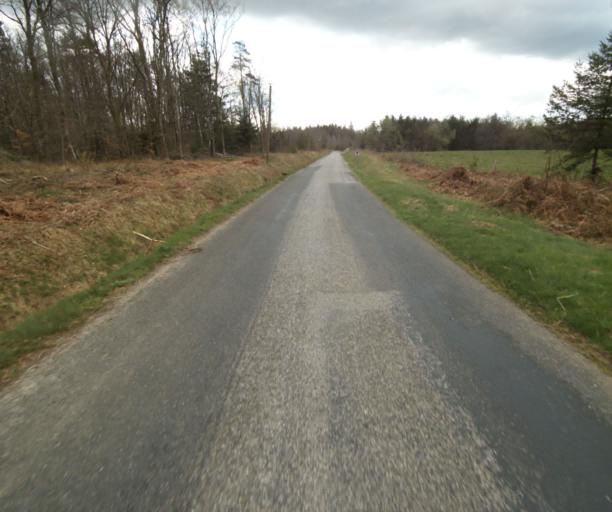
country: FR
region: Limousin
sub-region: Departement de la Correze
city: Correze
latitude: 45.2643
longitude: 1.9037
